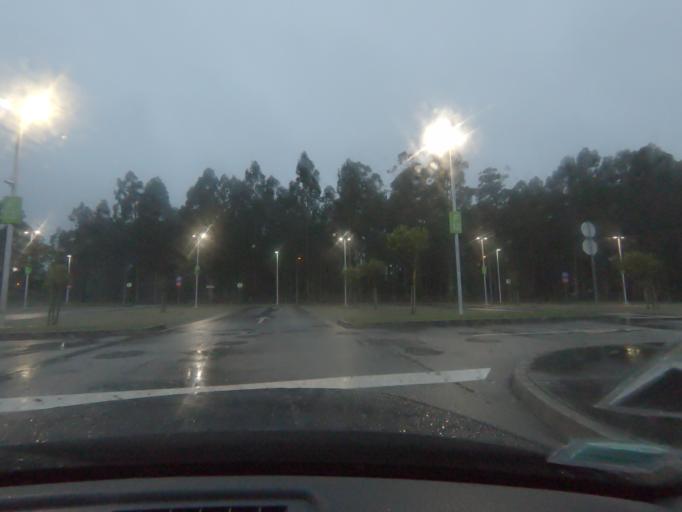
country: PT
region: Porto
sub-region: Matosinhos
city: Lavra
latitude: 41.2976
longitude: -8.7070
